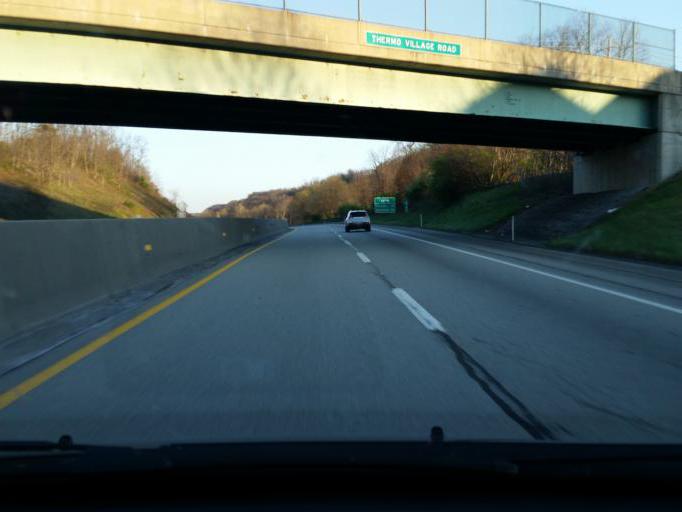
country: US
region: Pennsylvania
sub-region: Westmoreland County
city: New Stanton
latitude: 40.2154
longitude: -79.5957
